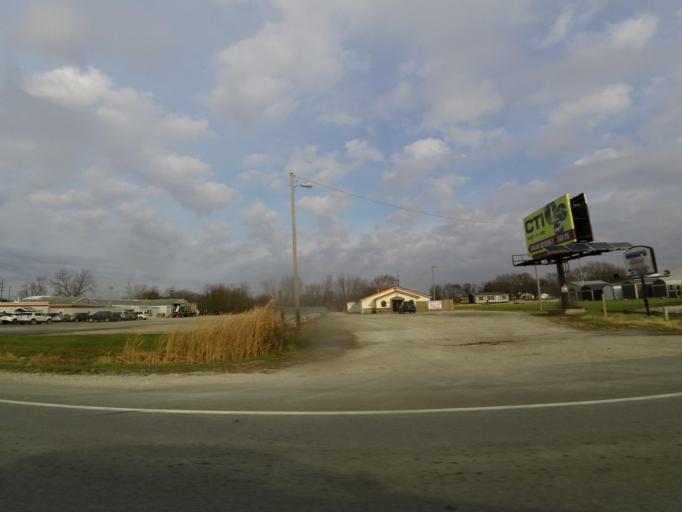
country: US
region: Illinois
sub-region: Christian County
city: Pana
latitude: 39.3895
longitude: -89.0609
